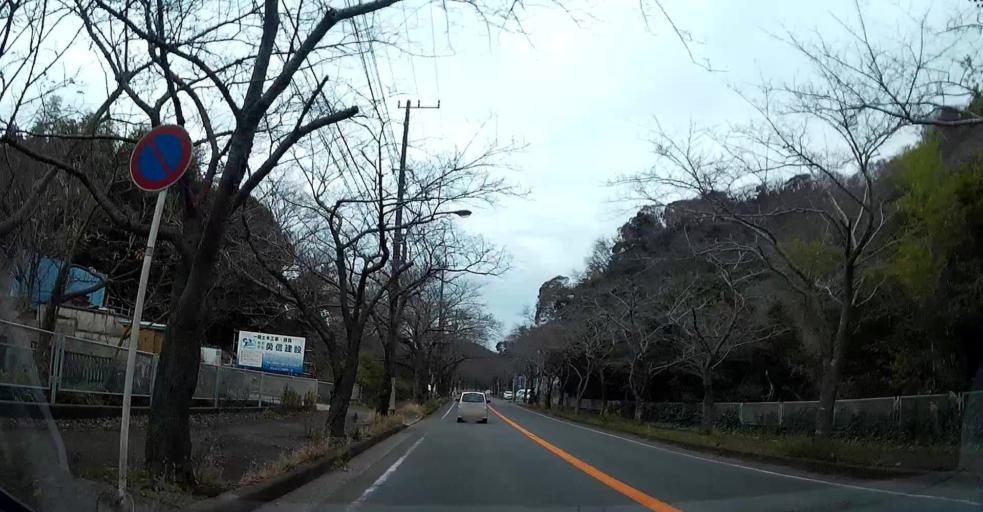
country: JP
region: Kanagawa
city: Yokosuka
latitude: 35.2194
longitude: 139.6700
